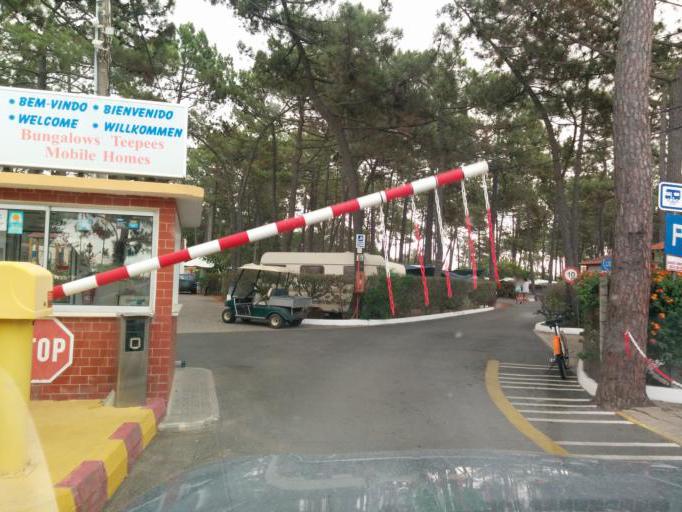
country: PT
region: Beja
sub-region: Odemira
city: Vila Nova de Milfontes
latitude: 37.7320
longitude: -8.7829
